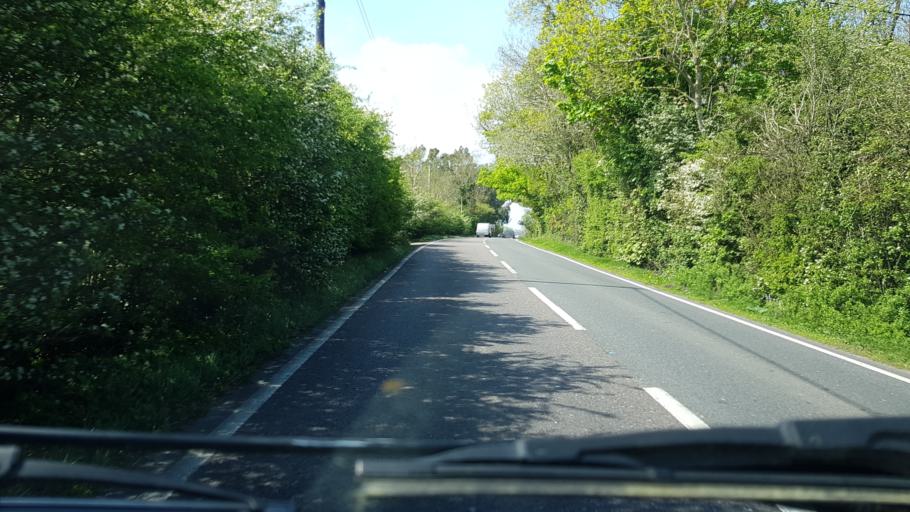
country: GB
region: England
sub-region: Kent
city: Paddock Wood
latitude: 51.1147
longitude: 0.3863
